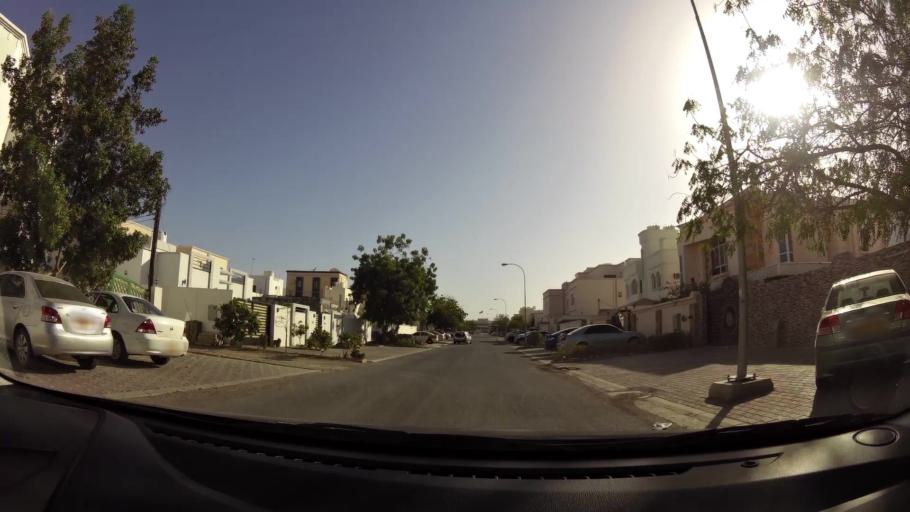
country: OM
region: Muhafazat Masqat
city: As Sib al Jadidah
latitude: 23.5972
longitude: 58.2132
